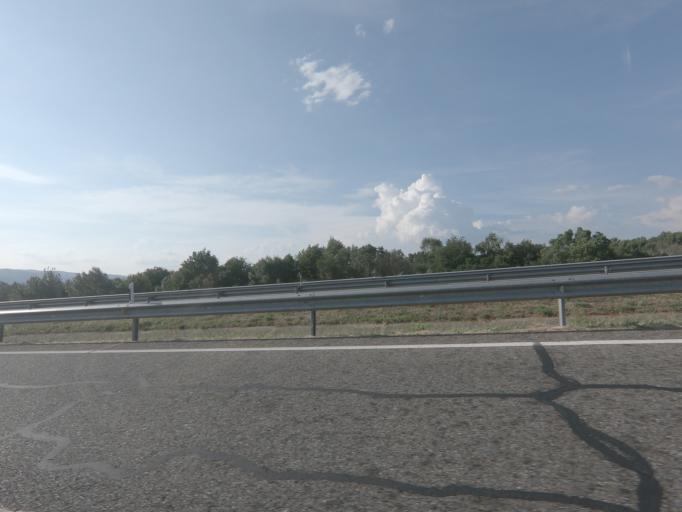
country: ES
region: Galicia
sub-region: Provincia de Ourense
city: Verin
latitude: 41.9227
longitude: -7.4679
